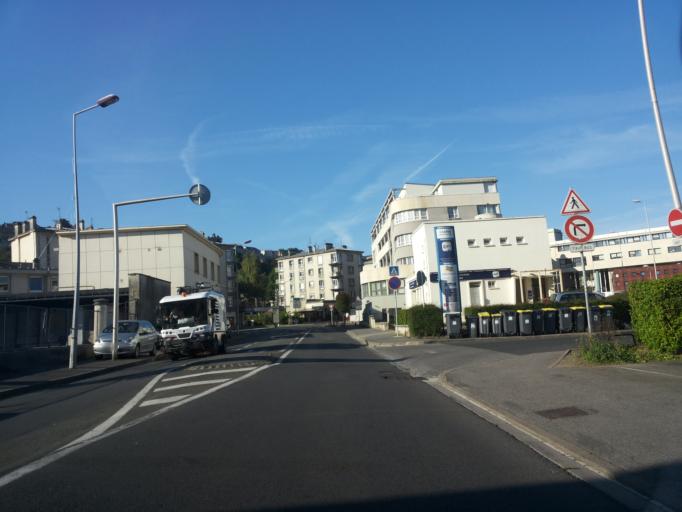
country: FR
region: Picardie
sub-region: Departement de l'Aisne
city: Laon
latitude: 49.5704
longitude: 3.6274
